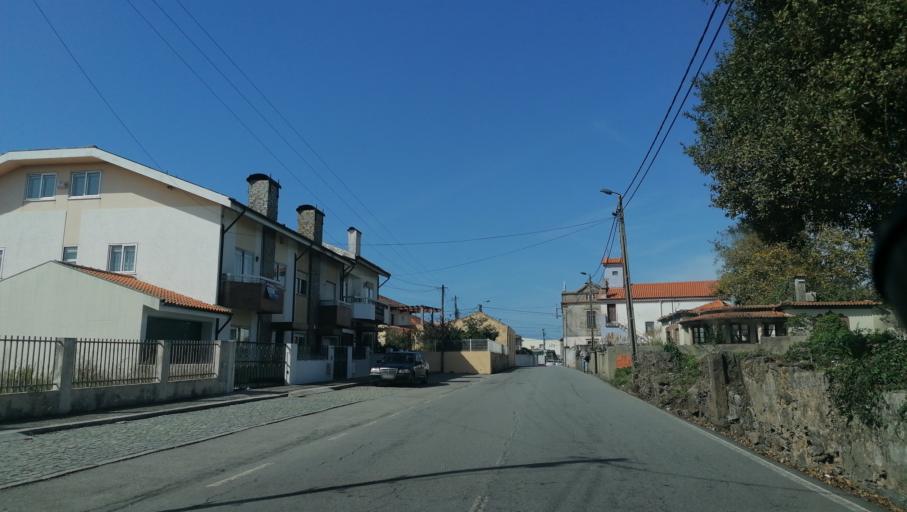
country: PT
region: Aveiro
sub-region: Espinho
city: Silvalde
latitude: 41.0032
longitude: -8.6223
